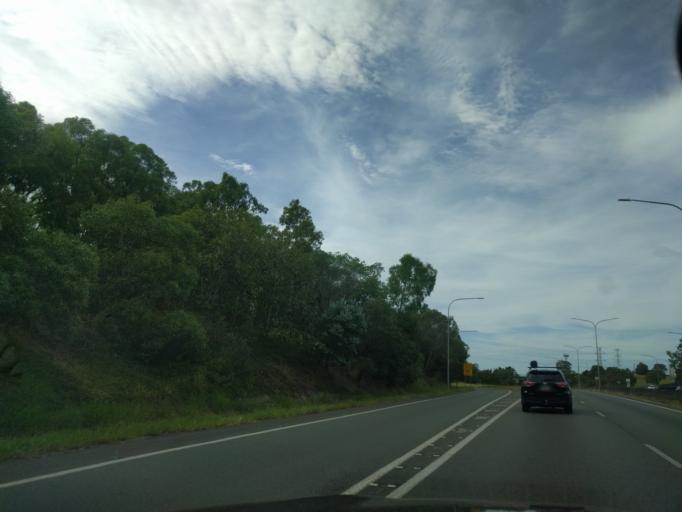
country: AU
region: Queensland
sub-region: Brisbane
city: Seventeen Mile Rocks
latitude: -27.5562
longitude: 152.9403
